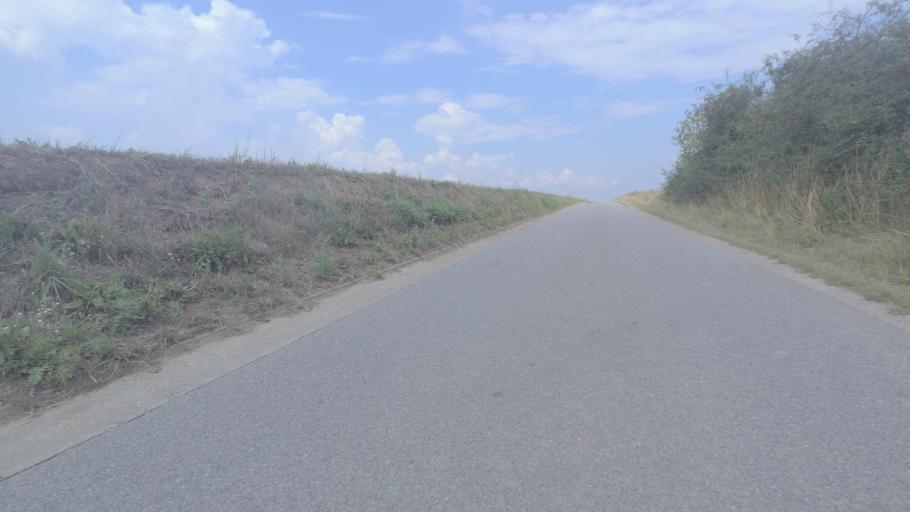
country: DE
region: Mecklenburg-Vorpommern
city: Borrentin
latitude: 53.8414
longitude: 12.9453
